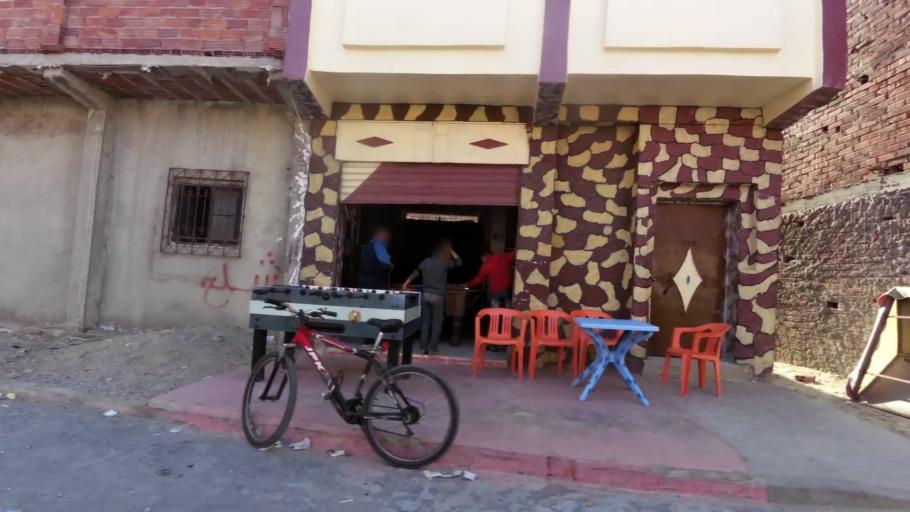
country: MA
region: Tanger-Tetouan
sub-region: Tetouan
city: Martil
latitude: 35.6102
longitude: -5.2750
